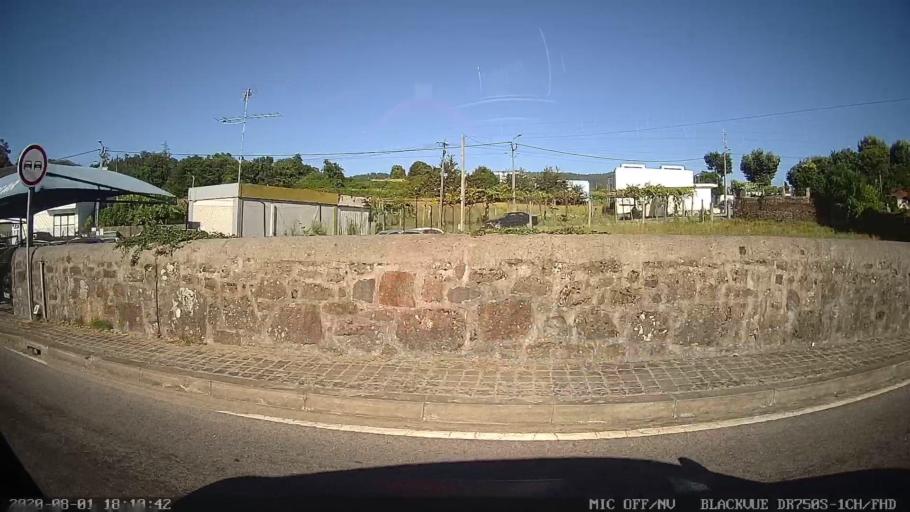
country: PT
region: Porto
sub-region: Santo Tirso
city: Sao Miguel do Couto
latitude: 41.3027
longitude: -8.4709
